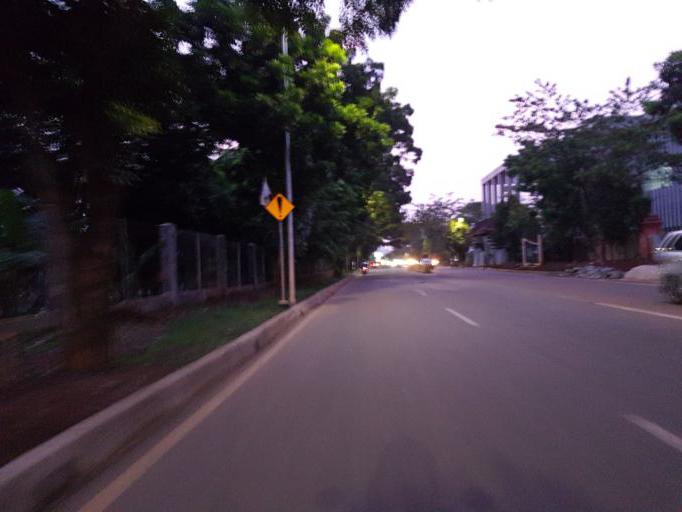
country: ID
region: West Java
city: Serpong
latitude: -6.3279
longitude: 106.6726
